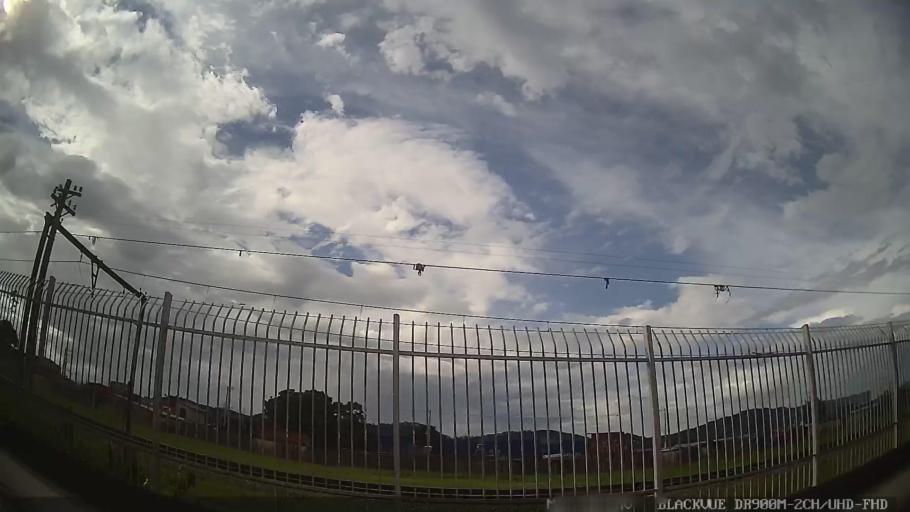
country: BR
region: Sao Paulo
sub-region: Mogi das Cruzes
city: Mogi das Cruzes
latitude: -23.5368
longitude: -46.2263
